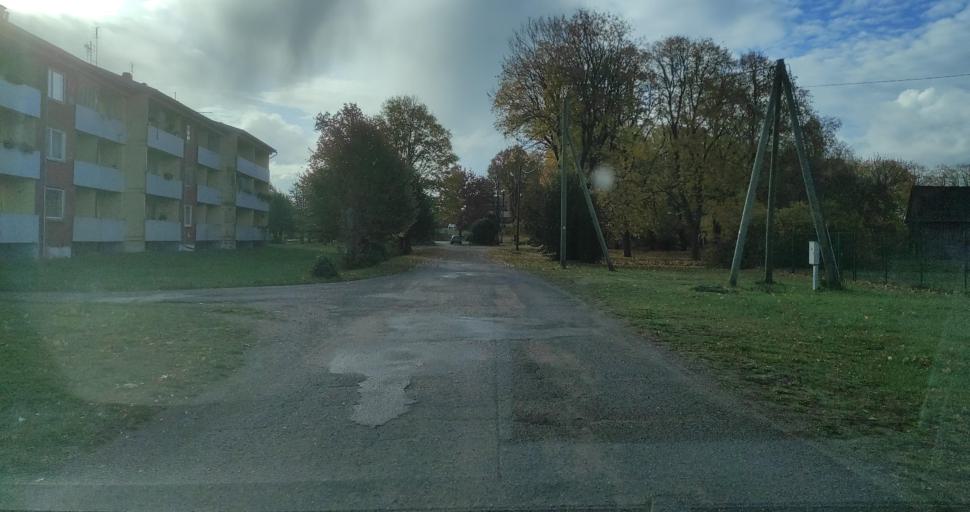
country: LV
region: Skrunda
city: Skrunda
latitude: 56.6834
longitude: 22.0485
